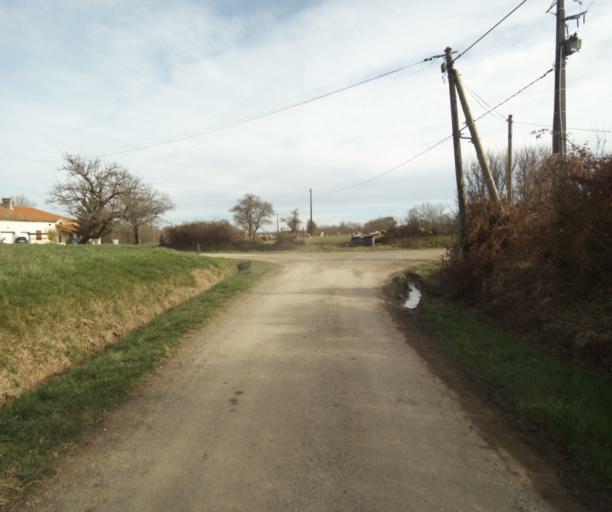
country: FR
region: Aquitaine
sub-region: Departement des Landes
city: Gabarret
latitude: 43.9677
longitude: 0.0448
